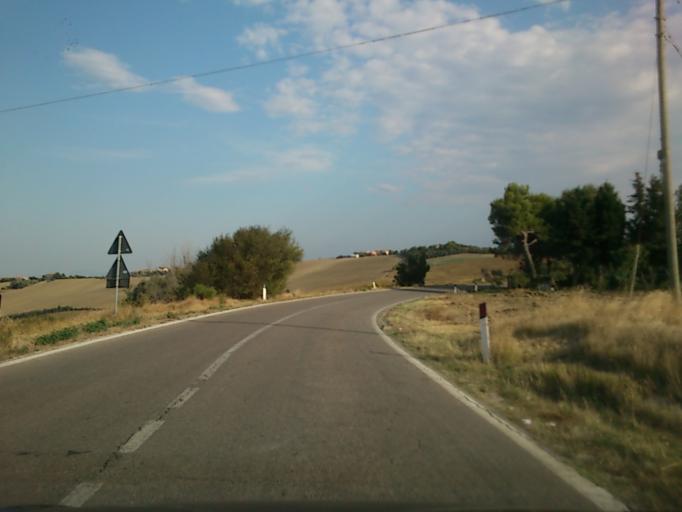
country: IT
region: The Marches
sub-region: Provincia di Pesaro e Urbino
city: San Costanzo
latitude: 43.7885
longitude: 13.0673
